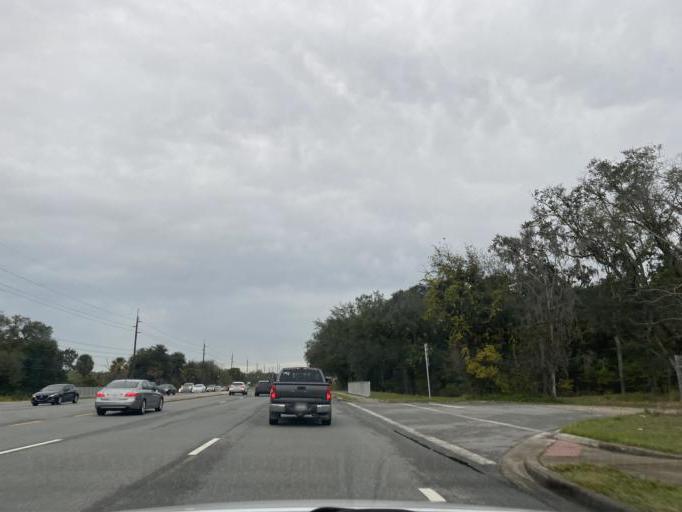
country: US
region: Florida
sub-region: Orange County
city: Oakland
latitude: 28.5512
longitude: -81.6200
